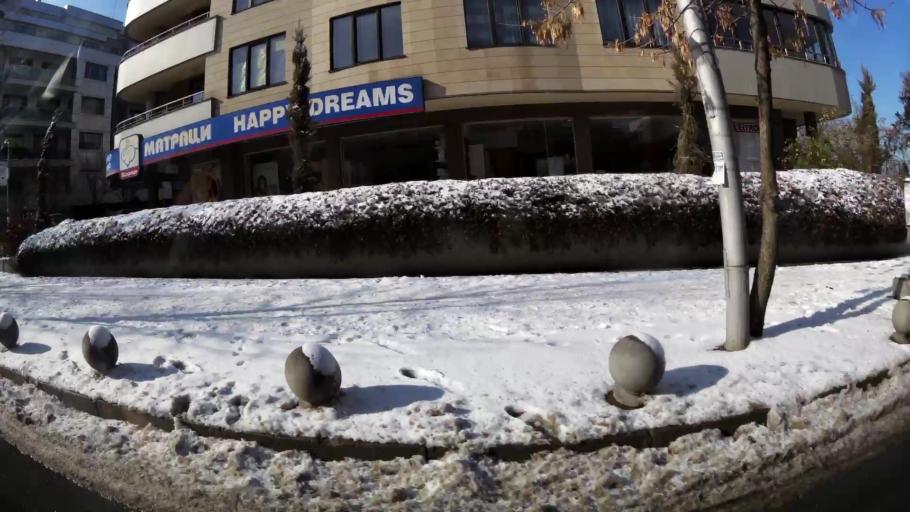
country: BG
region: Sofia-Capital
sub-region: Stolichna Obshtina
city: Sofia
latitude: 42.6682
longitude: 23.3140
